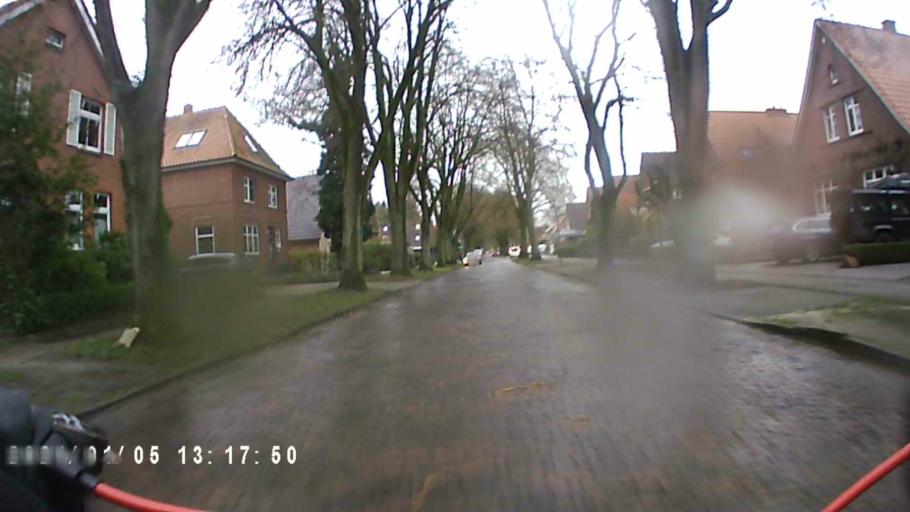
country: DE
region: Lower Saxony
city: Leer
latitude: 53.2355
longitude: 7.4465
